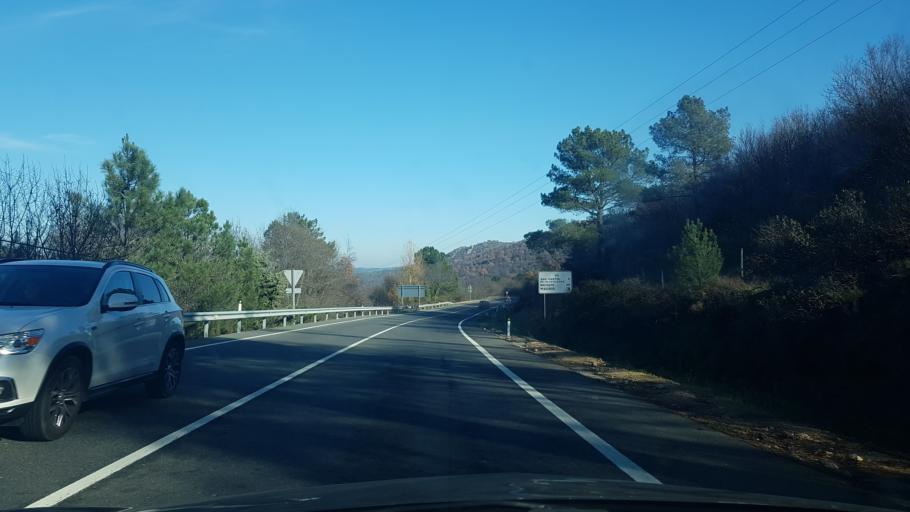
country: ES
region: Castille and Leon
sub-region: Provincia de Avila
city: Navahondilla
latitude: 40.3104
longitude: -4.5167
